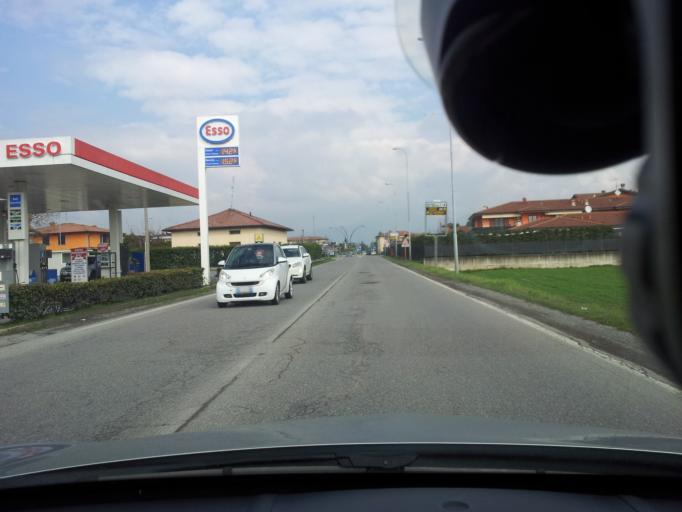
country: IT
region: Lombardy
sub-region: Provincia di Bergamo
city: Bolgare
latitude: 45.6322
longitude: 9.8079
